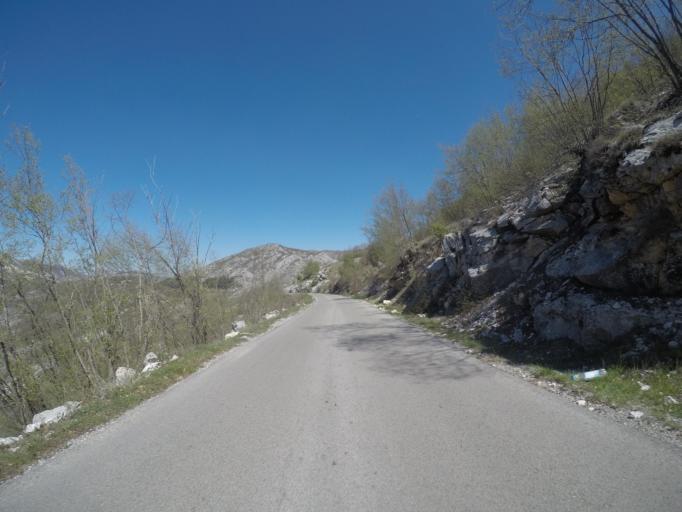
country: ME
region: Cetinje
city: Cetinje
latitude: 42.4517
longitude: 18.8736
